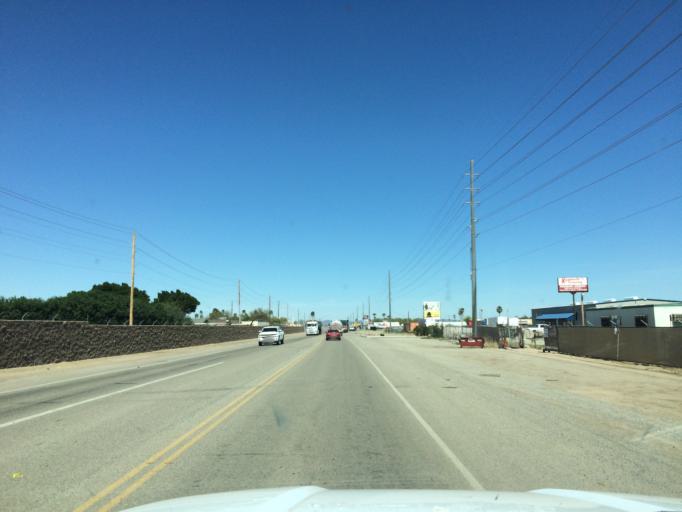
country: US
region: Arizona
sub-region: Yuma County
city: Yuma
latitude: 32.6520
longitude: -114.5811
